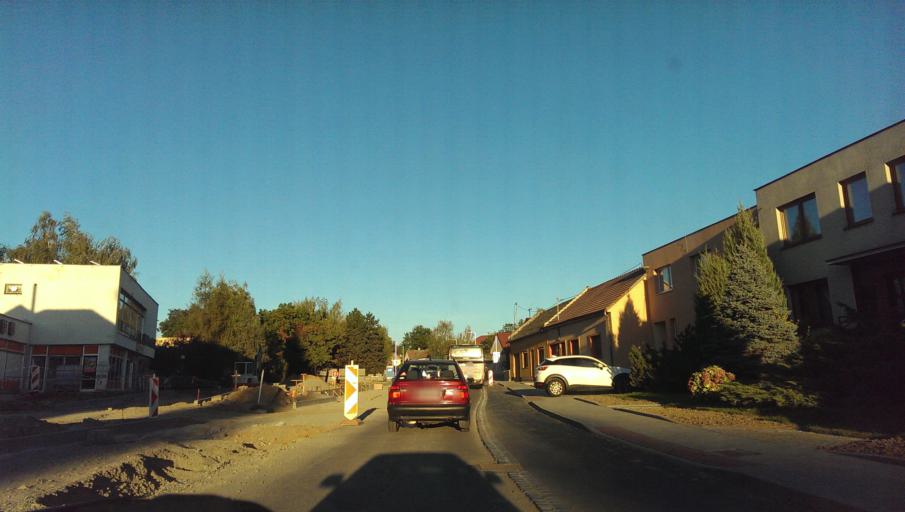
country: CZ
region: Zlin
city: Zlechov
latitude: 49.0729
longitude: 17.3808
